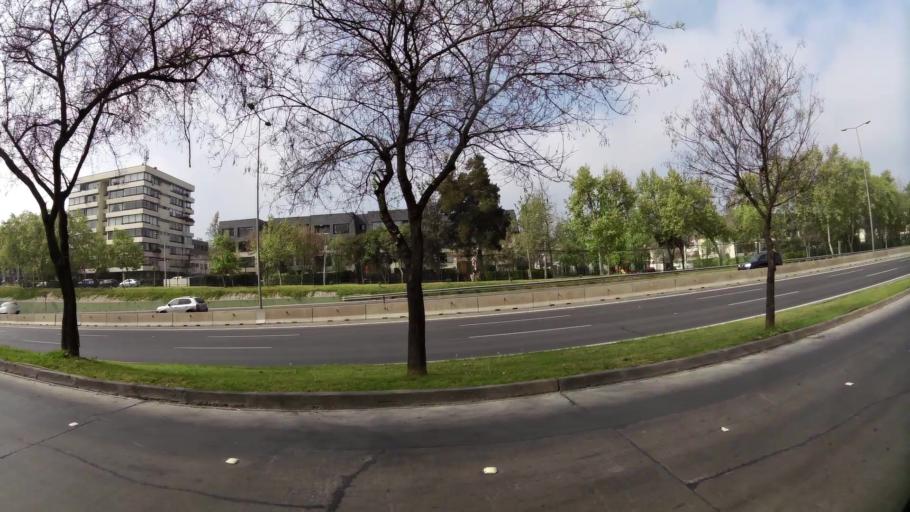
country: CL
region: Santiago Metropolitan
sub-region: Provincia de Santiago
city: Villa Presidente Frei, Nunoa, Santiago, Chile
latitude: -33.3900
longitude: -70.5496
